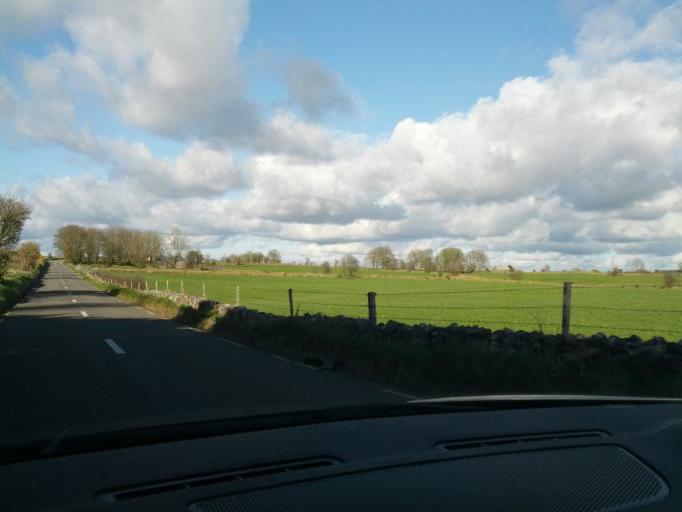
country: IE
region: Connaught
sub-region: Roscommon
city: Castlerea
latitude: 53.5712
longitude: -8.5672
